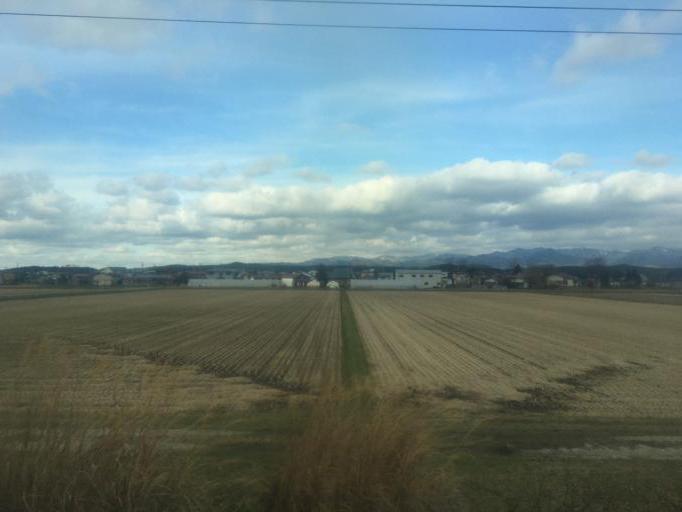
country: JP
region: Akita
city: Noshiromachi
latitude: 40.2142
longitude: 140.1590
